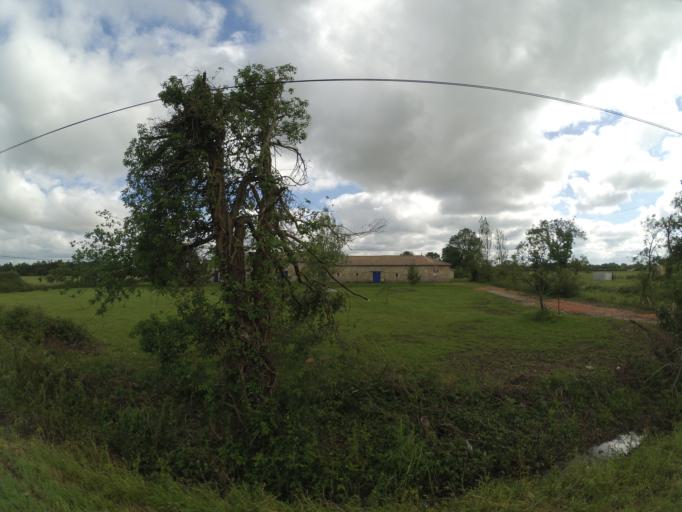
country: FR
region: Aquitaine
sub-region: Departement de la Gironde
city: Ludon-Medoc
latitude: 44.9936
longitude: -0.5885
